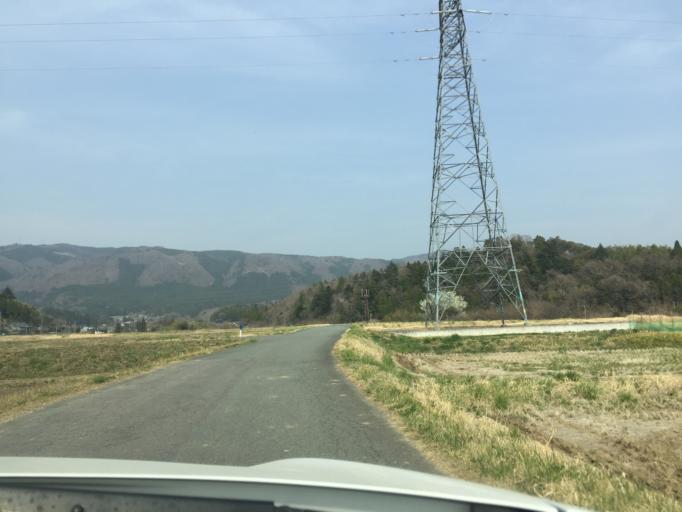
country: JP
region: Fukushima
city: Iwaki
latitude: 37.0230
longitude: 140.7310
